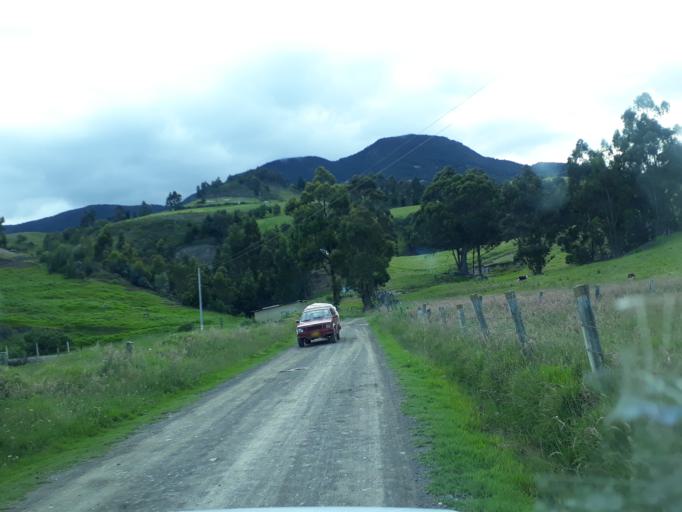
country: CO
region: Cundinamarca
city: Carmen de Carupa
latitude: 5.3087
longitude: -73.9079
